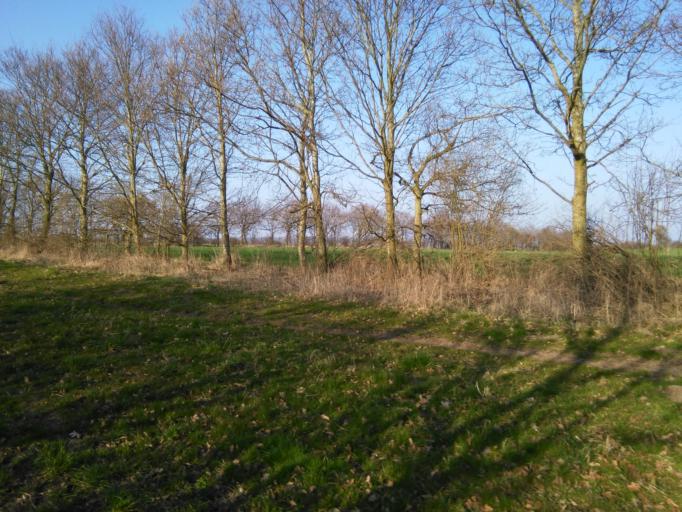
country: DK
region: Central Jutland
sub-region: Arhus Kommune
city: Marslet
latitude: 56.0722
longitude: 10.1861
